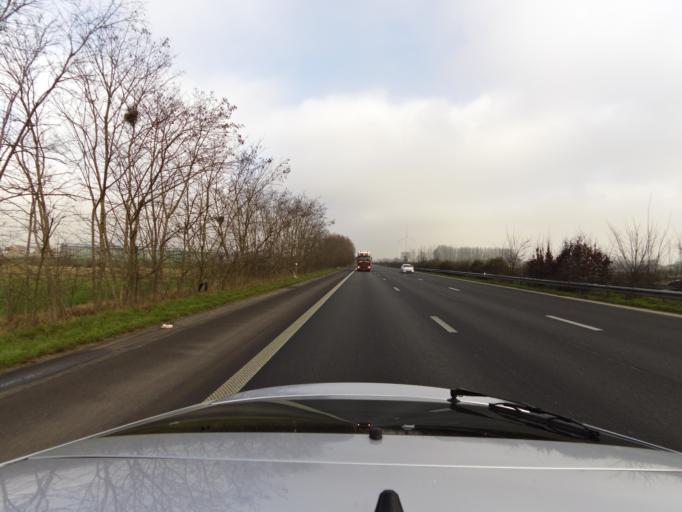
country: BE
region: Flanders
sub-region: Provincie West-Vlaanderen
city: Izegem
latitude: 50.8844
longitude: 3.1728
